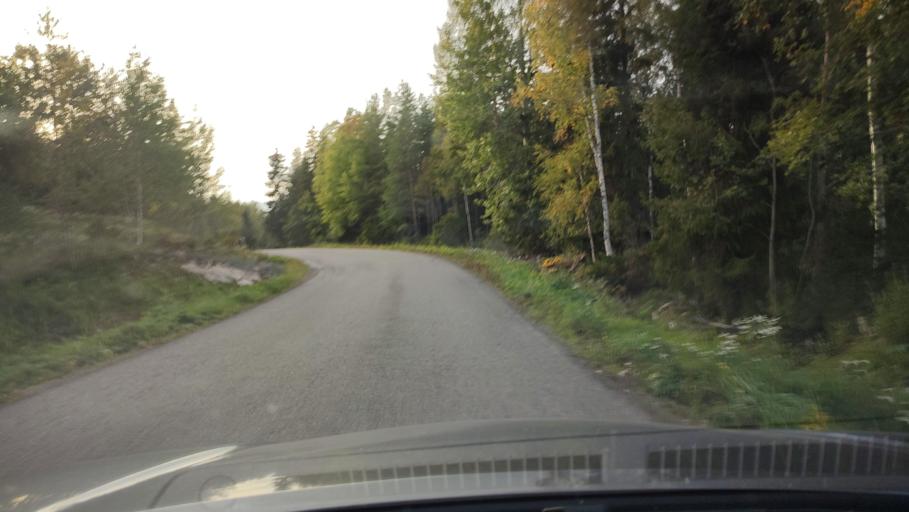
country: FI
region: Ostrobothnia
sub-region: Sydosterbotten
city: Kristinestad
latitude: 62.1510
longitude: 21.5430
